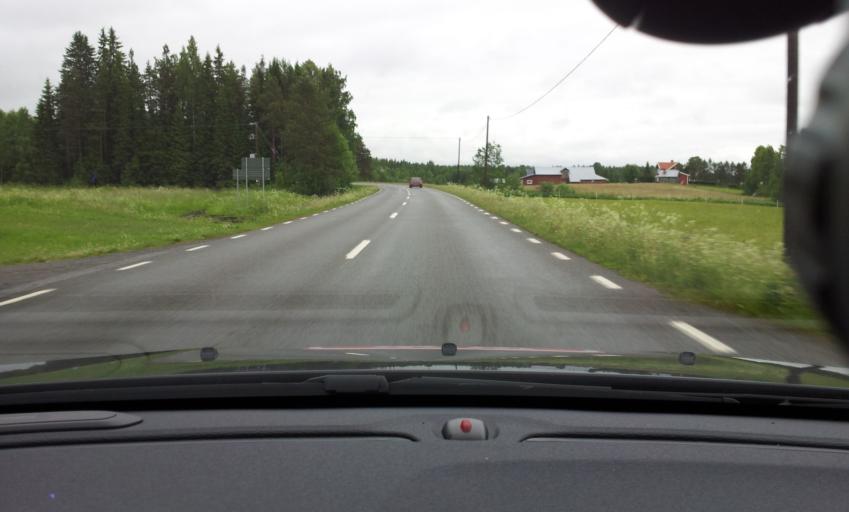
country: SE
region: Jaemtland
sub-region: Stroemsunds Kommun
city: Stroemsund
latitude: 63.5341
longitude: 15.4476
